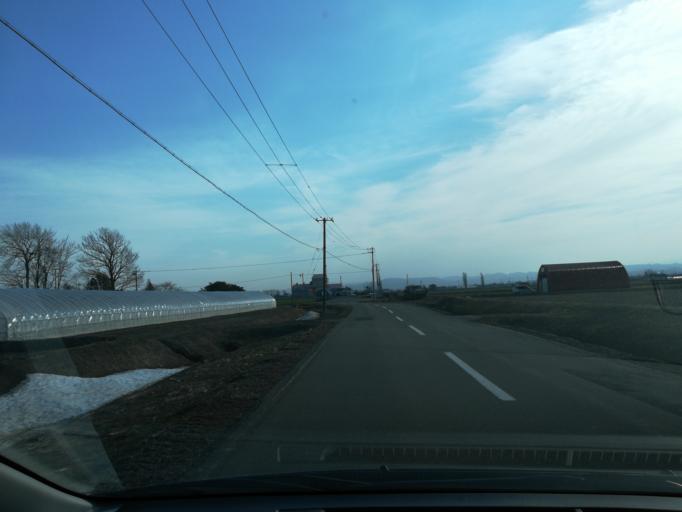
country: JP
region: Hokkaido
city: Iwamizawa
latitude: 43.1915
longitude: 141.7094
